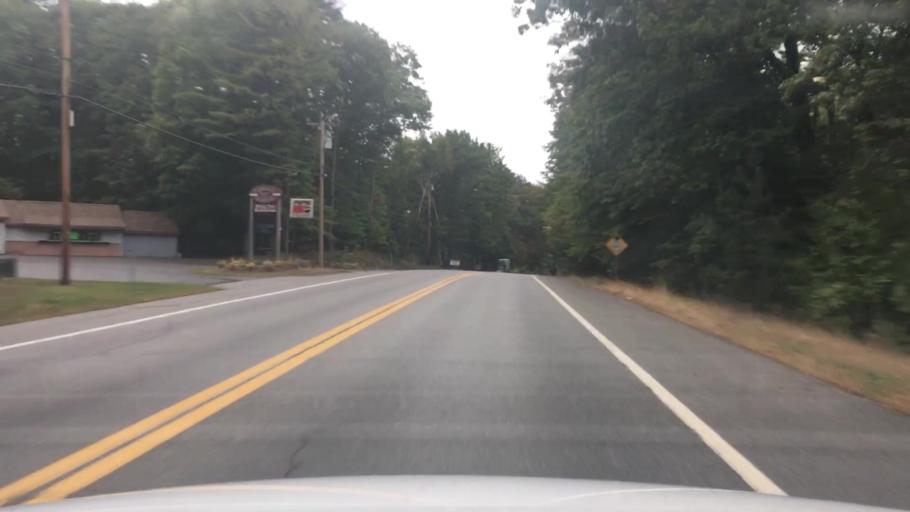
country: US
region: Maine
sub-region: Kennebec County
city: Rome
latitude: 44.5231
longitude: -69.8828
